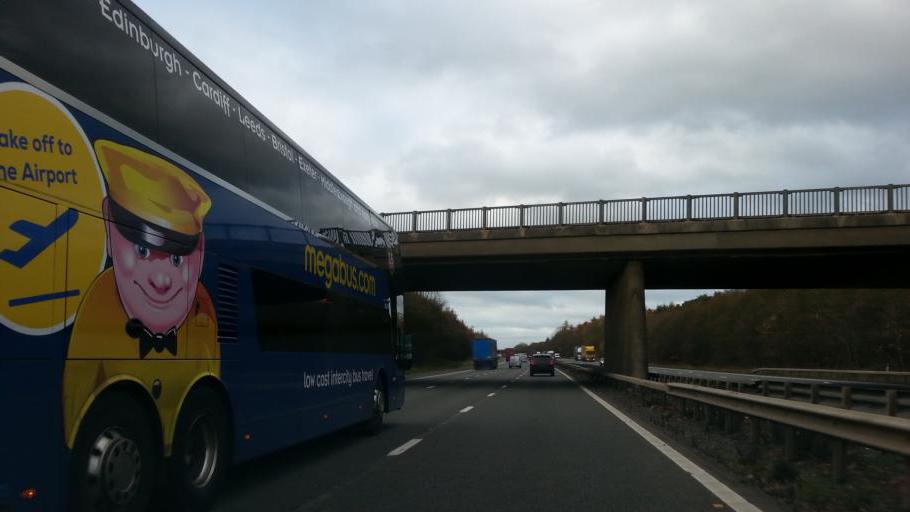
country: GB
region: England
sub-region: Warwickshire
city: Long Lawford
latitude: 52.4314
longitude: -1.3317
